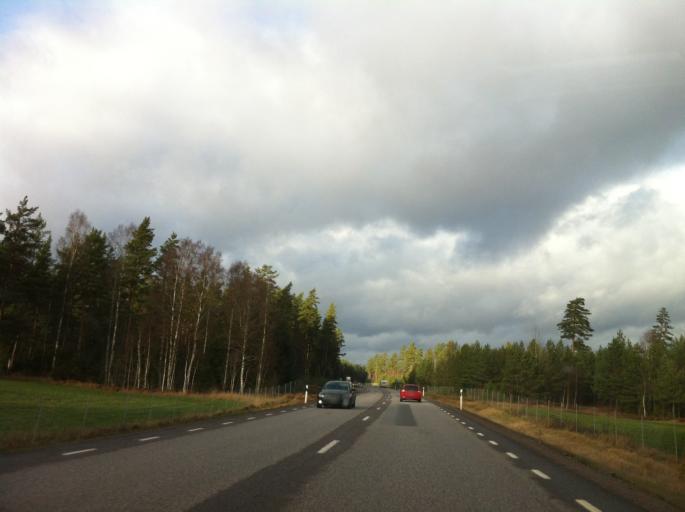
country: SE
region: Kalmar
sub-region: Vimmerby Kommun
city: Vimmerby
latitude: 57.6130
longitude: 15.8445
